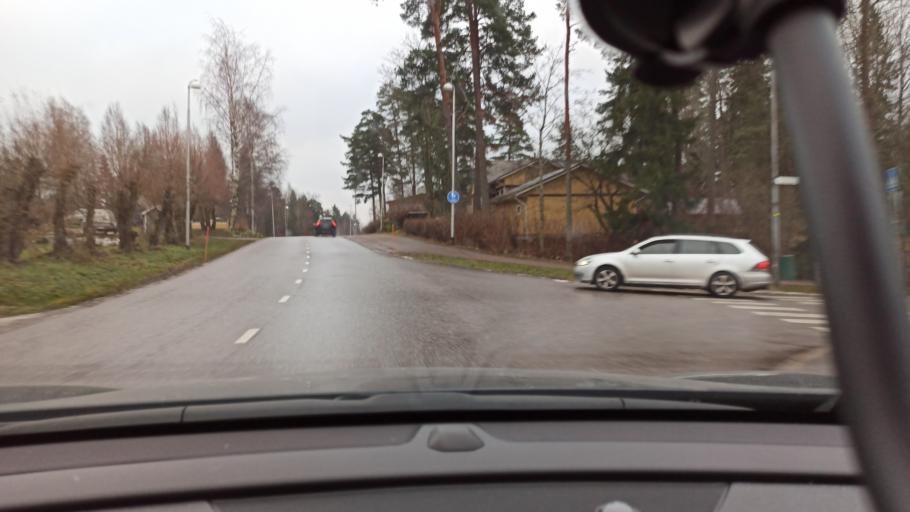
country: FI
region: Uusimaa
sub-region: Helsinki
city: Kirkkonummi
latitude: 60.1310
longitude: 24.4317
